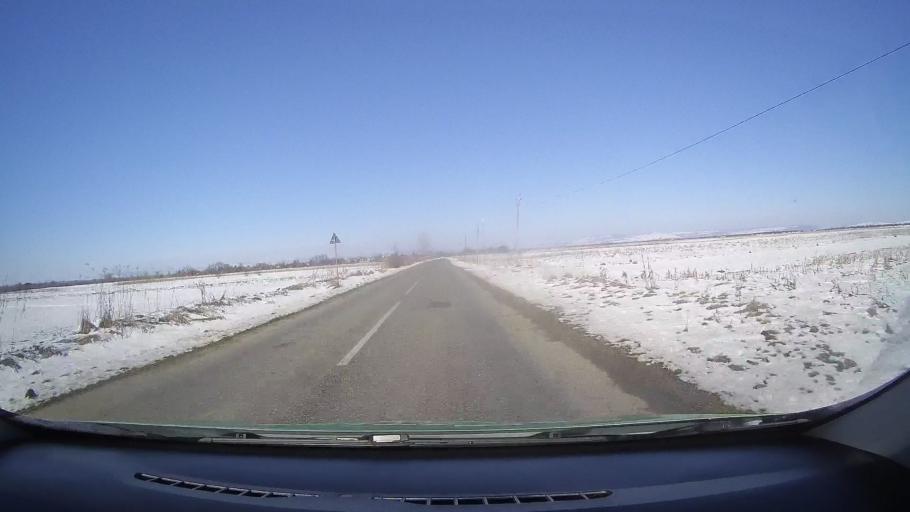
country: RO
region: Brasov
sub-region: Comuna Harseni
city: Harseni
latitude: 45.7444
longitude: 25.0182
